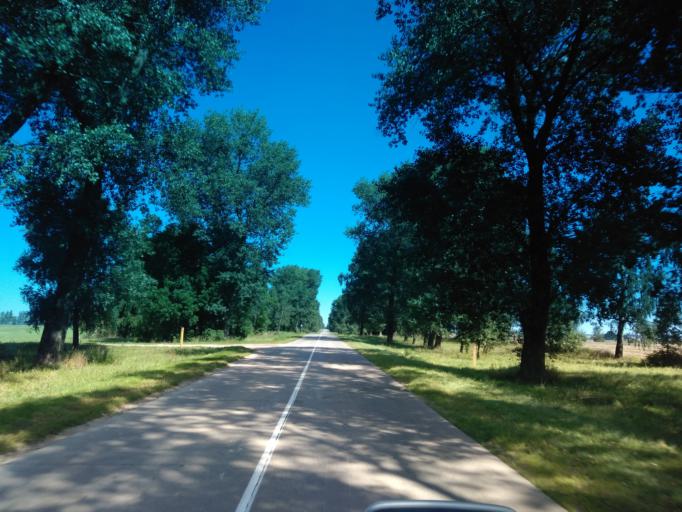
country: BY
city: Fanipol
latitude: 53.6758
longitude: 27.3532
